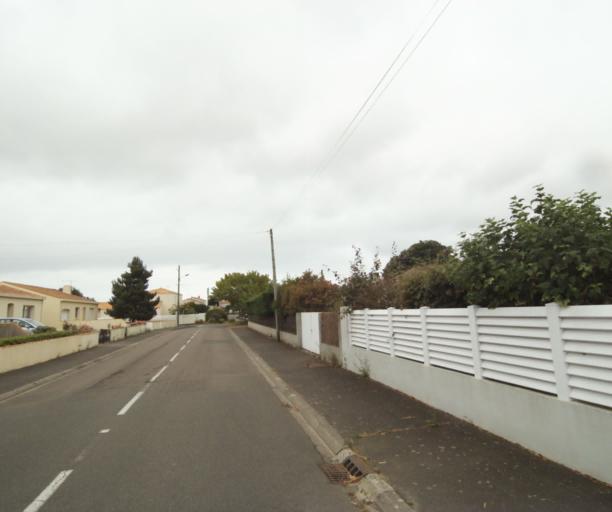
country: FR
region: Pays de la Loire
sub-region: Departement de la Vendee
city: Chateau-d'Olonne
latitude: 46.5029
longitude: -1.7499
